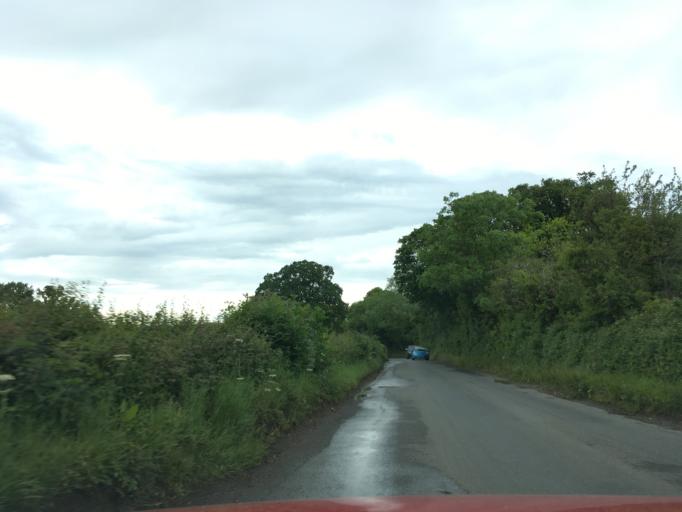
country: GB
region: England
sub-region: Gloucestershire
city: Tetbury
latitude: 51.6017
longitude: -2.1846
